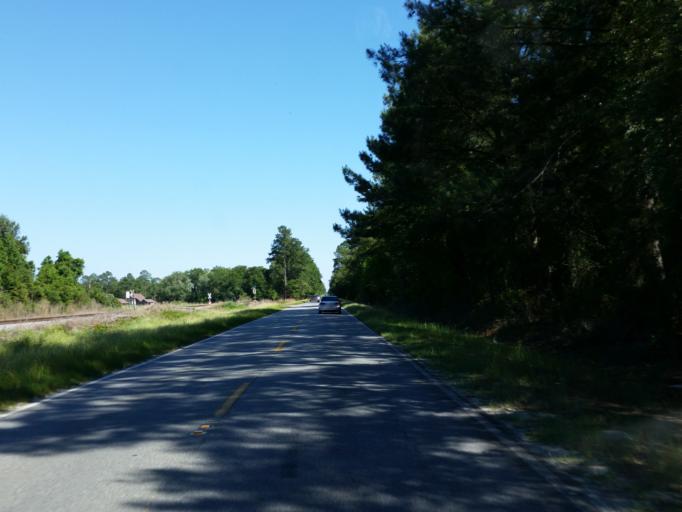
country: US
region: Georgia
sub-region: Echols County
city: Statenville
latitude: 30.6705
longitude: -83.1653
